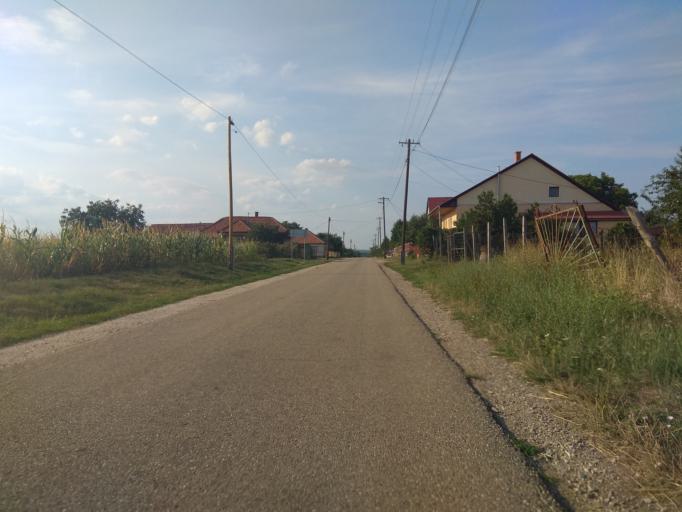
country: HU
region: Borsod-Abauj-Zemplen
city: Harsany
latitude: 47.9152
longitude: 20.7410
